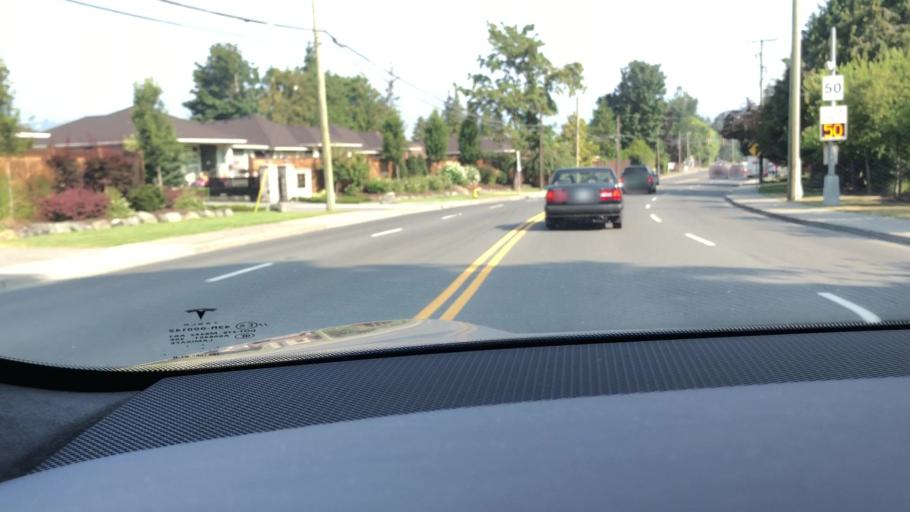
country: CA
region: British Columbia
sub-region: Fraser Valley Regional District
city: Chilliwack
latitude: 49.1208
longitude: -121.9596
